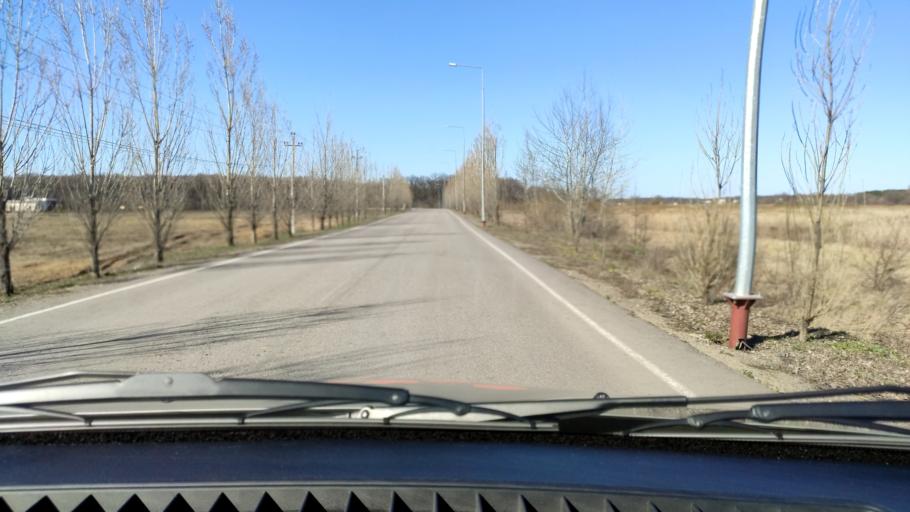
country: RU
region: Voronezj
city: Somovo
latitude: 51.6840
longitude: 39.3424
